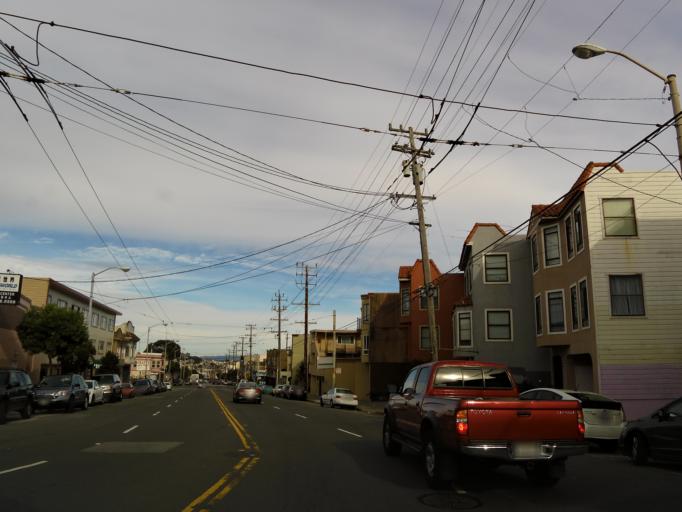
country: US
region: California
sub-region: San Mateo County
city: Daly City
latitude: 37.7118
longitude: -122.4457
